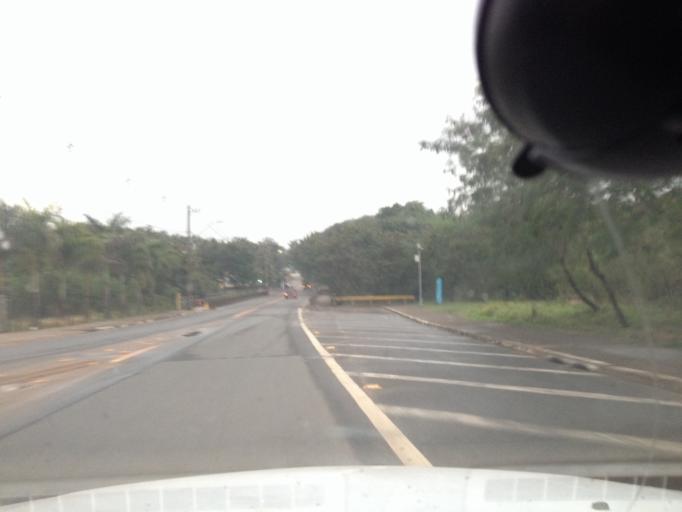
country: BR
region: Sao Paulo
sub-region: Salto
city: Salto
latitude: -23.1959
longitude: -47.2685
